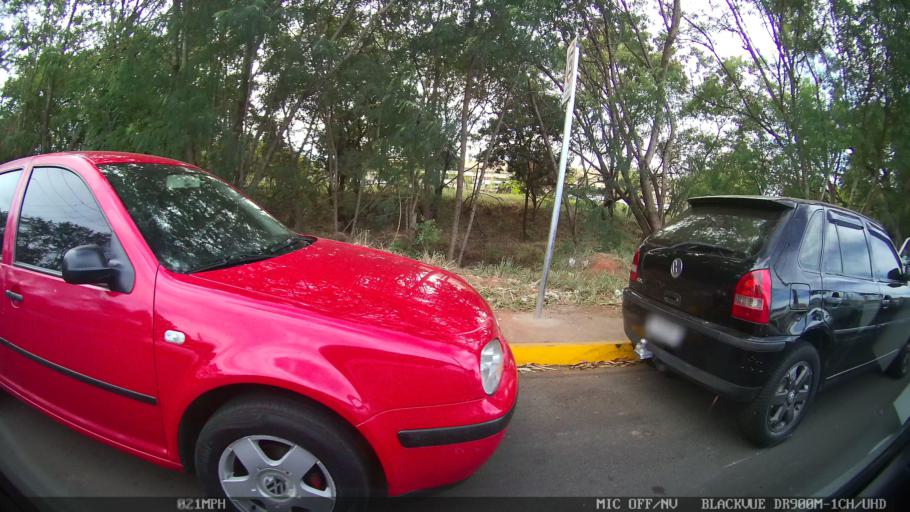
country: BR
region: Sao Paulo
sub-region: Catanduva
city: Catanduva
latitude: -21.1275
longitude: -48.9802
